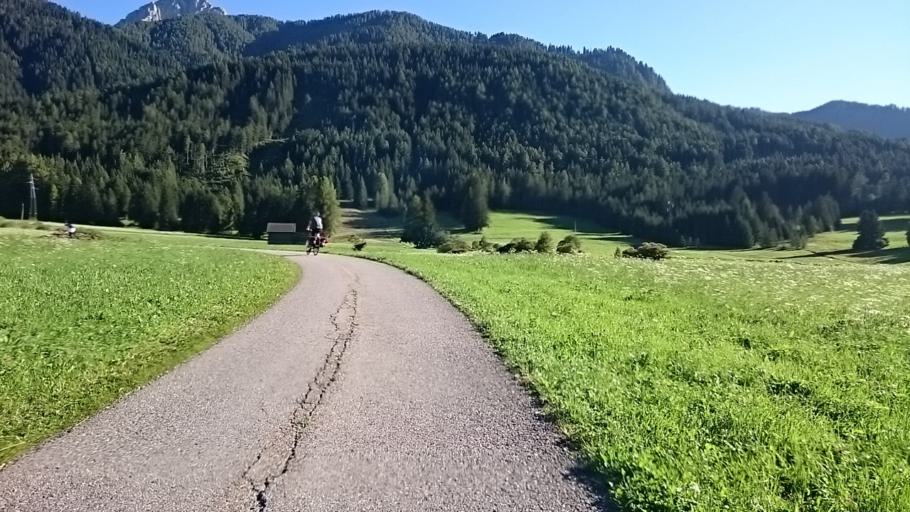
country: IT
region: Trentino-Alto Adige
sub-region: Bolzano
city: Villabassa
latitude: 46.7316
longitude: 12.1933
